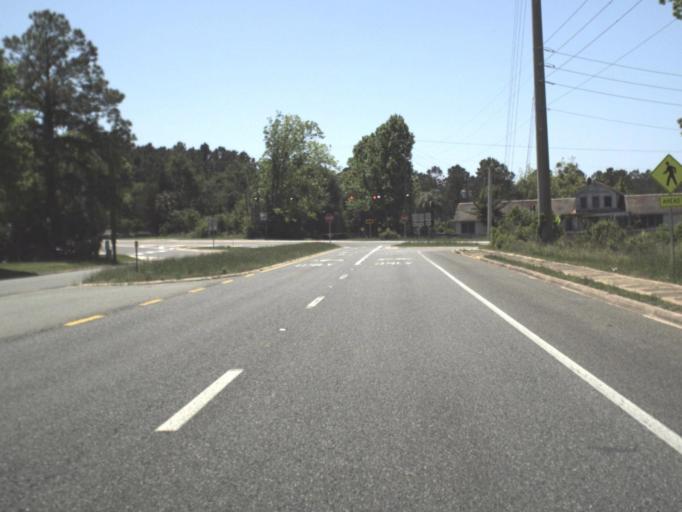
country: US
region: Florida
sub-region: Jefferson County
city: Monticello
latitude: 30.4122
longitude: -83.9114
